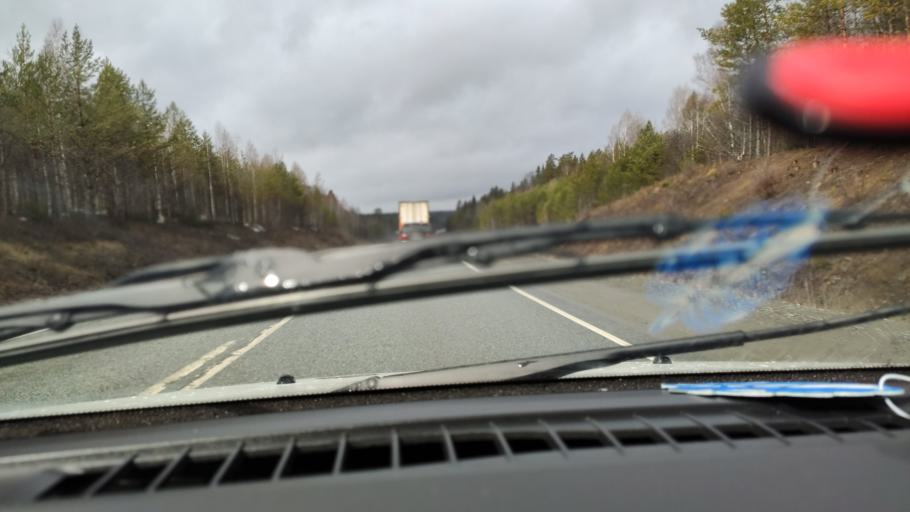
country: RU
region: Sverdlovsk
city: Atig
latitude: 56.8000
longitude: 59.3854
